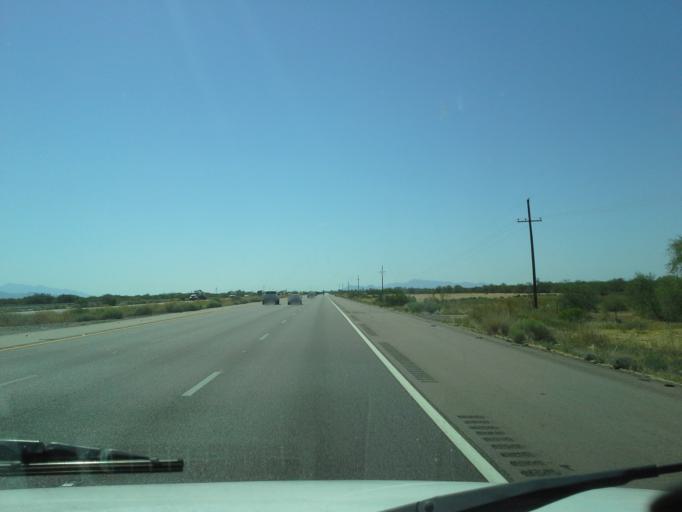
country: US
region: Arizona
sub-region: Pima County
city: Avra Valley
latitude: 32.6106
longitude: -111.3545
